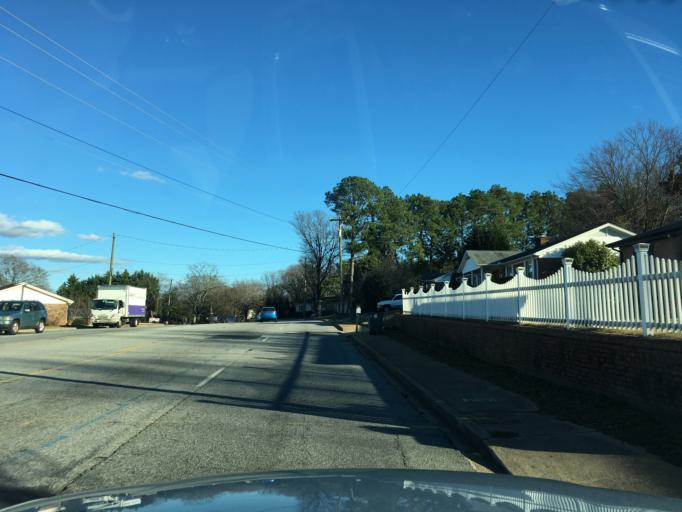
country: US
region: South Carolina
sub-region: Greenville County
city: Wade Hampton
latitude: 34.8722
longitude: -82.3340
